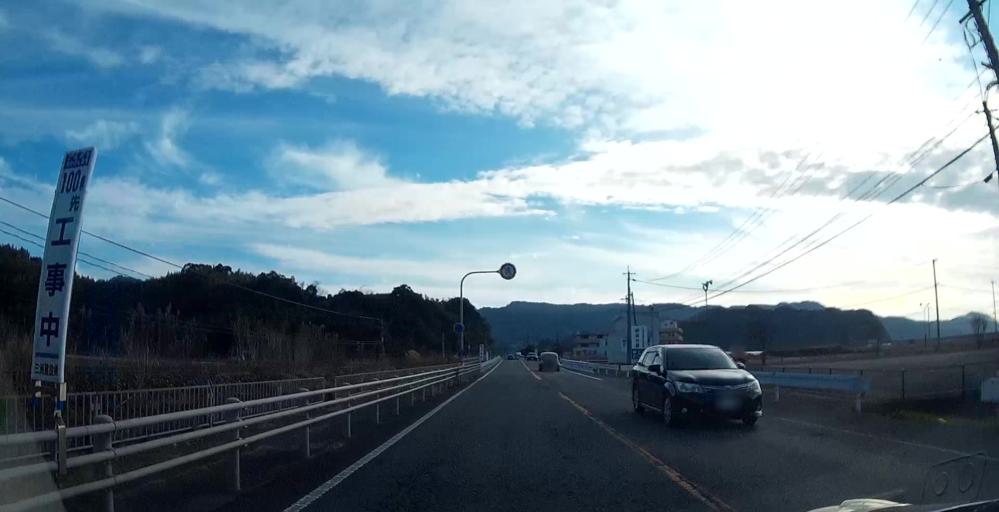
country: JP
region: Kumamoto
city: Uto
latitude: 32.6820
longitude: 130.5538
